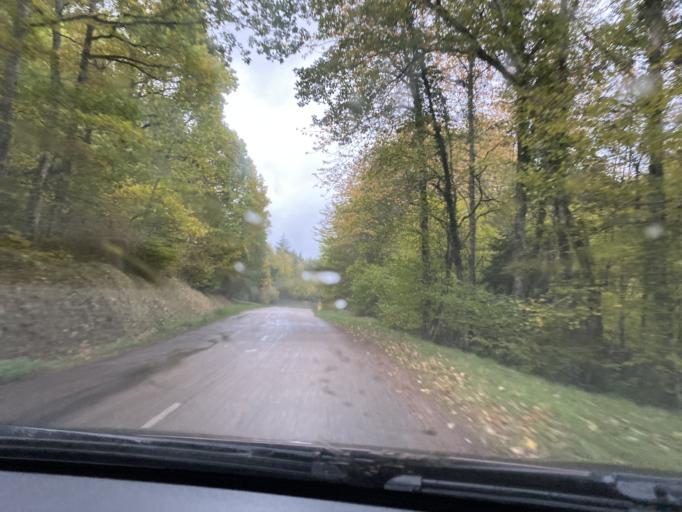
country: FR
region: Bourgogne
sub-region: Departement de la Cote-d'Or
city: Saulieu
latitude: 47.3520
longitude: 4.2405
